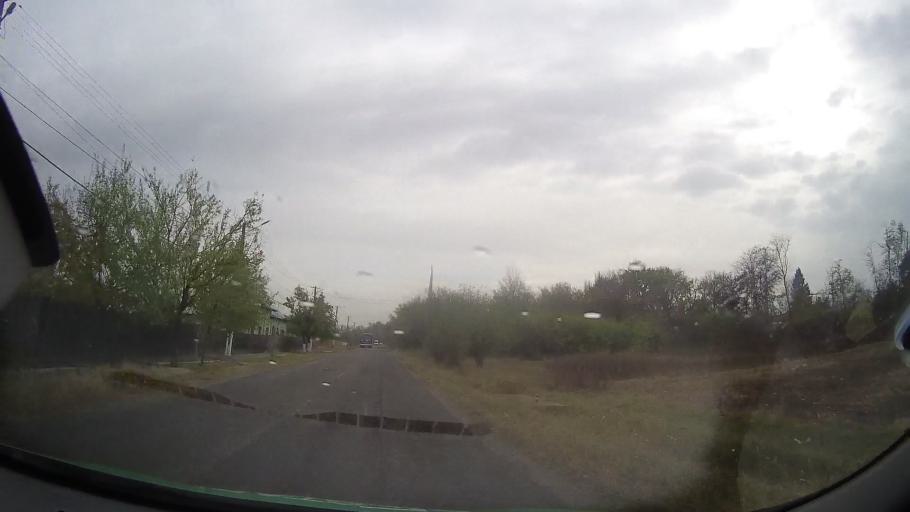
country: RO
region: Prahova
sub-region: Comuna Dumbrava
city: Dumbrava
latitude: 44.8644
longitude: 26.2032
